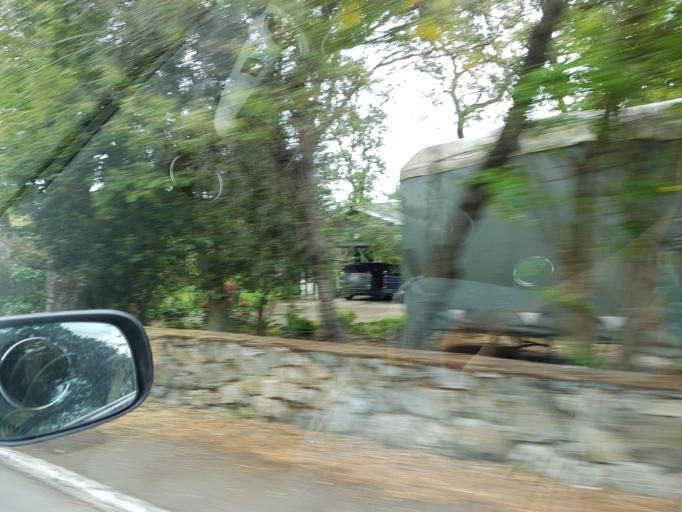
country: CA
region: British Columbia
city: Oak Bay
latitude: 48.4779
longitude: -123.3384
